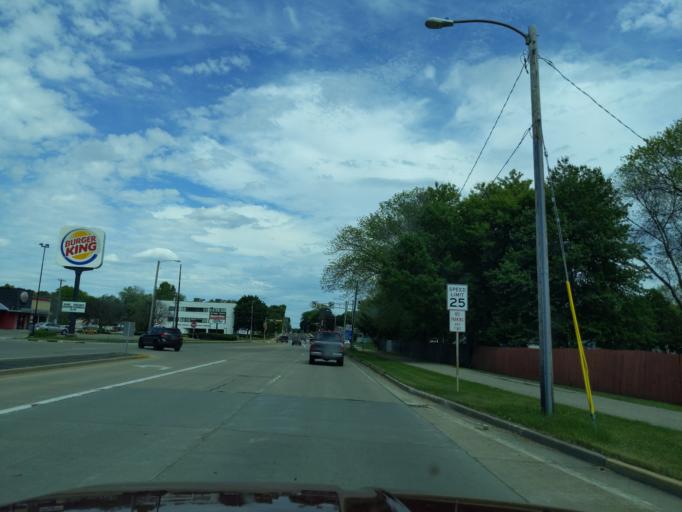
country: US
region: Wisconsin
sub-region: Dane County
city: Sun Prairie
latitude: 43.1874
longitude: -89.2282
